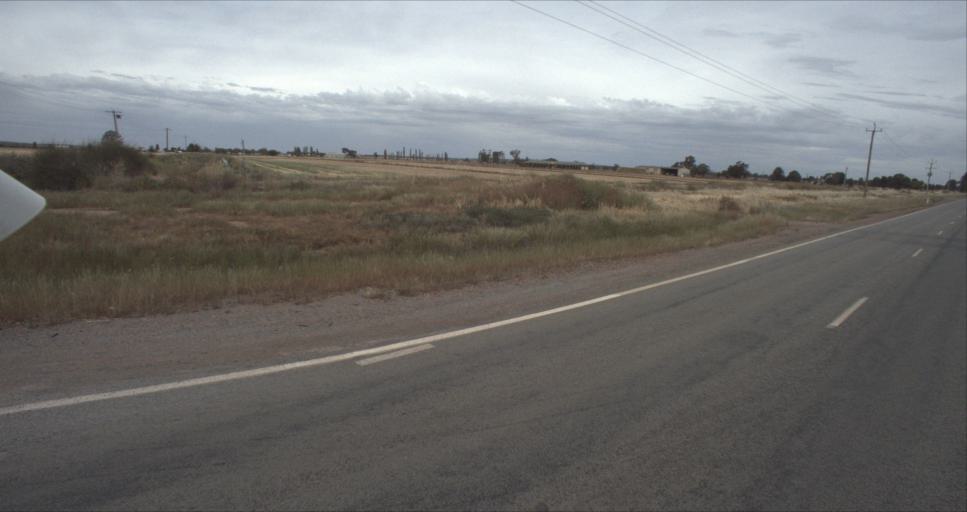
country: AU
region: New South Wales
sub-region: Leeton
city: Leeton
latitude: -34.5069
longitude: 146.4226
